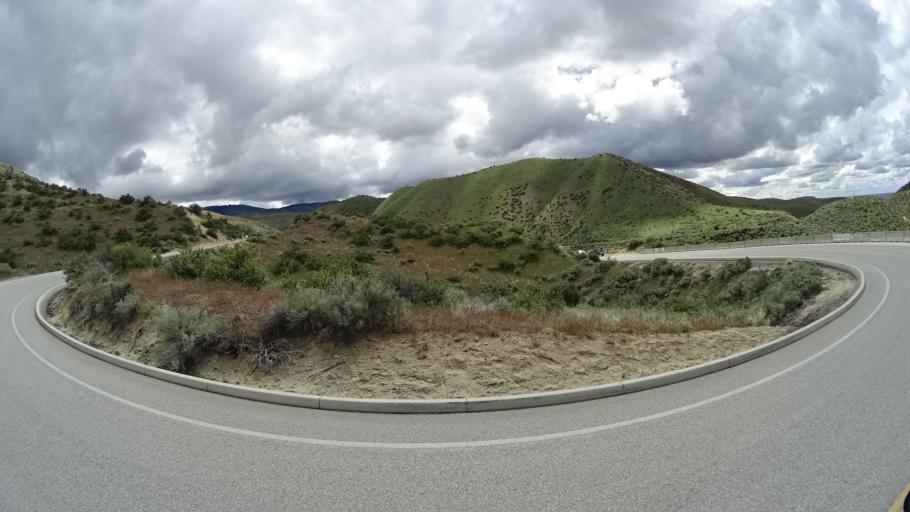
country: US
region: Idaho
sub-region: Ada County
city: Boise
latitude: 43.6894
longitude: -116.1858
